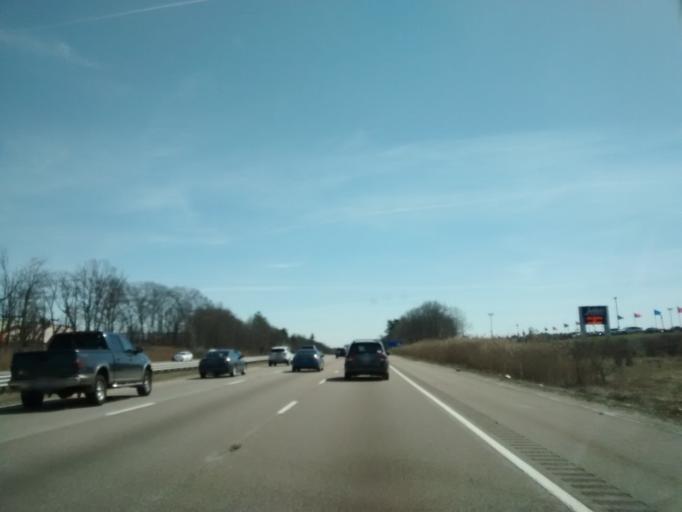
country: US
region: Massachusetts
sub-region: Norfolk County
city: Avon
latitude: 42.1357
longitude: -71.0646
